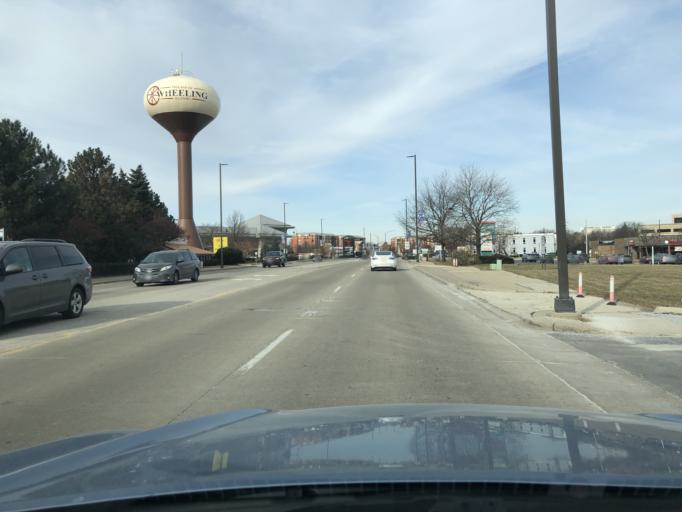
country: US
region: Illinois
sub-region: Cook County
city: Wheeling
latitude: 42.1380
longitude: -87.9059
